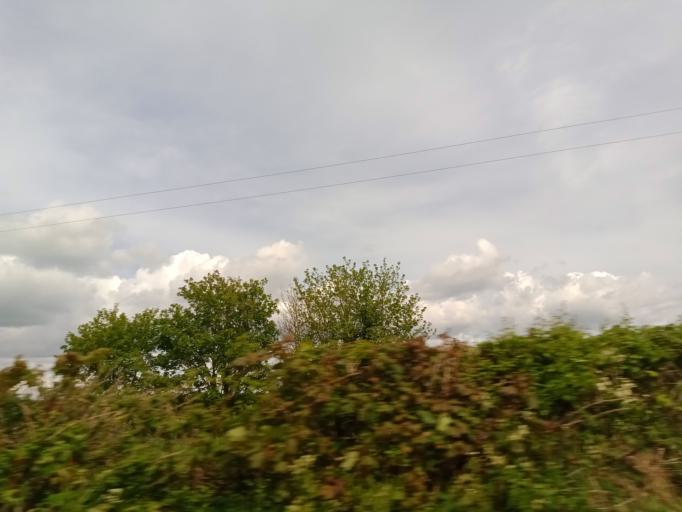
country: IE
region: Munster
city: Thurles
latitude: 52.6161
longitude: -7.7886
